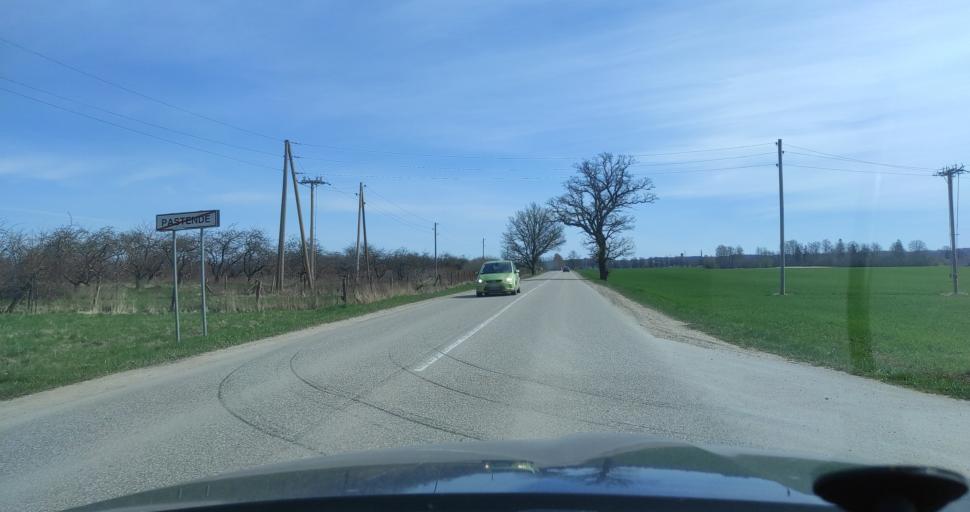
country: LV
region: Talsu Rajons
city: Talsi
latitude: 57.2277
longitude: 22.5293
